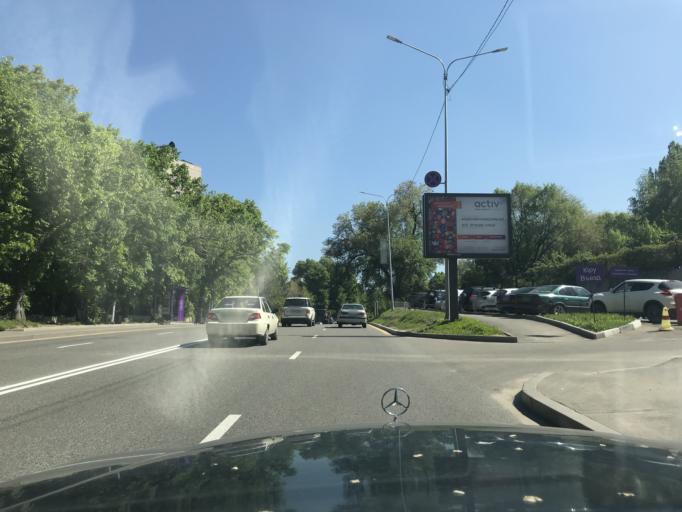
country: KZ
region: Almaty Qalasy
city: Almaty
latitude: 43.2342
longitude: 76.9399
